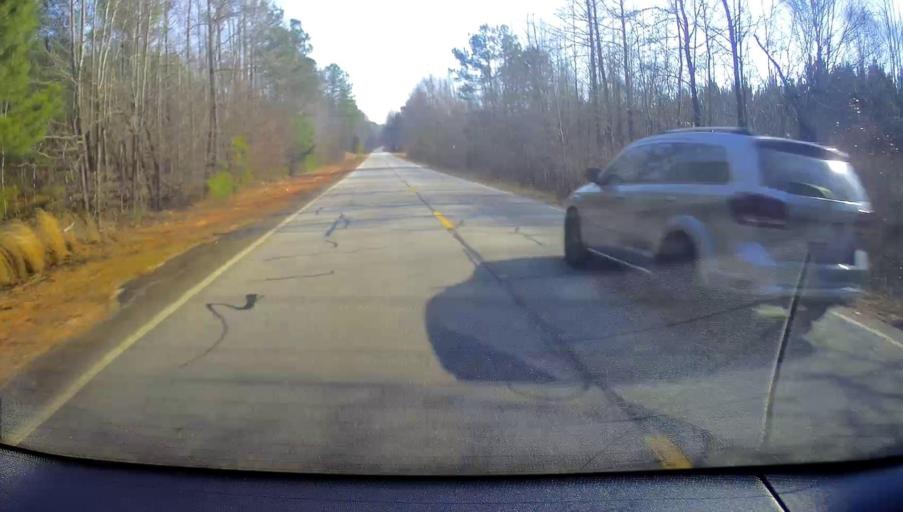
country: US
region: Georgia
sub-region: Butts County
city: Indian Springs
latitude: 33.1993
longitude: -83.8531
